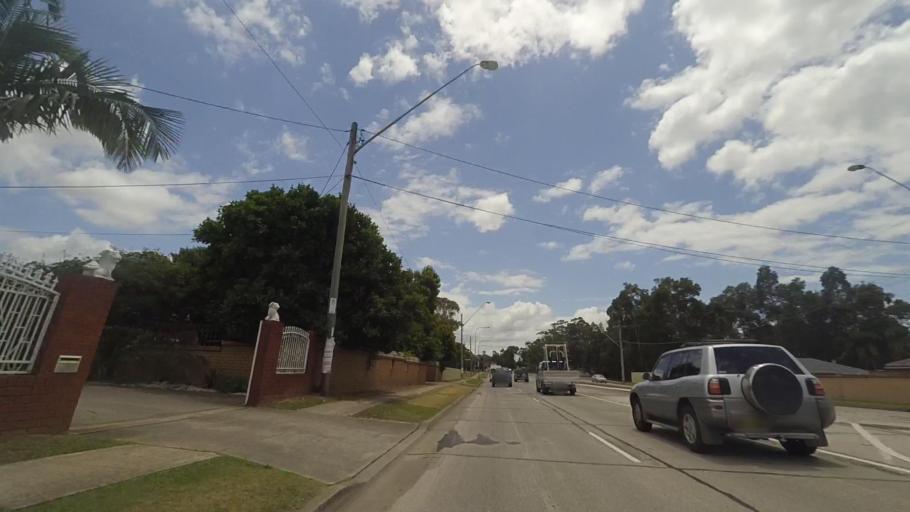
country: AU
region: New South Wales
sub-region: Fairfield
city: Fairfield Heights
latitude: -33.8760
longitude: 150.9253
